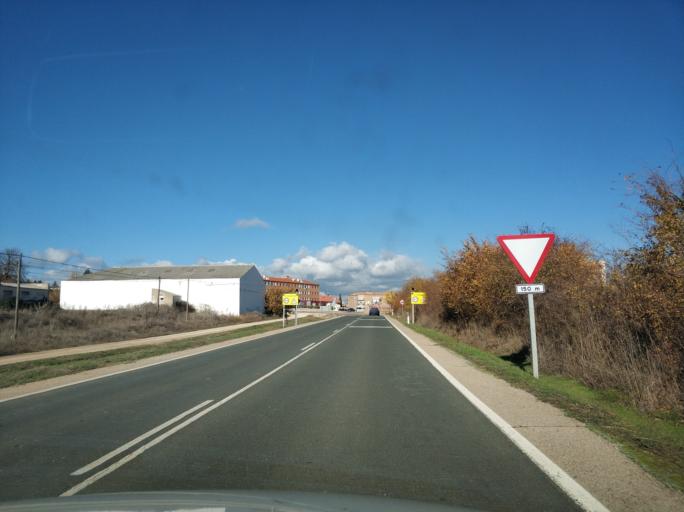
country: ES
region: Castille and Leon
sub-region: Provincia de Soria
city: Almazan
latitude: 41.4781
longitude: -2.5295
